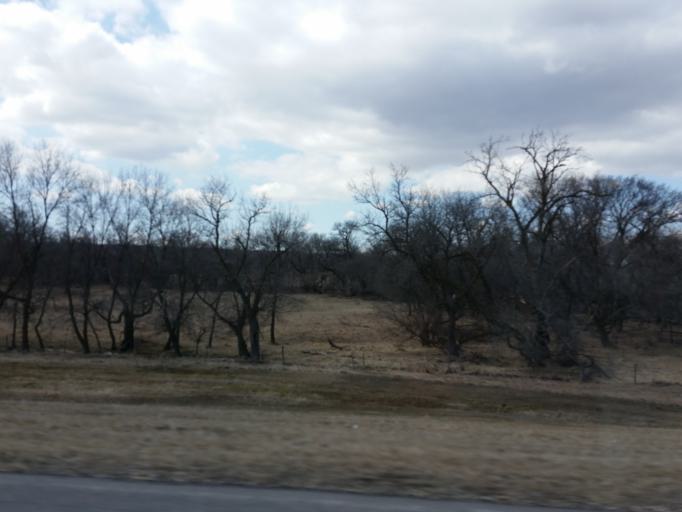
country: US
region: South Dakota
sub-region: Roberts County
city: Sisseton
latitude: 45.4453
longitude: -96.9897
